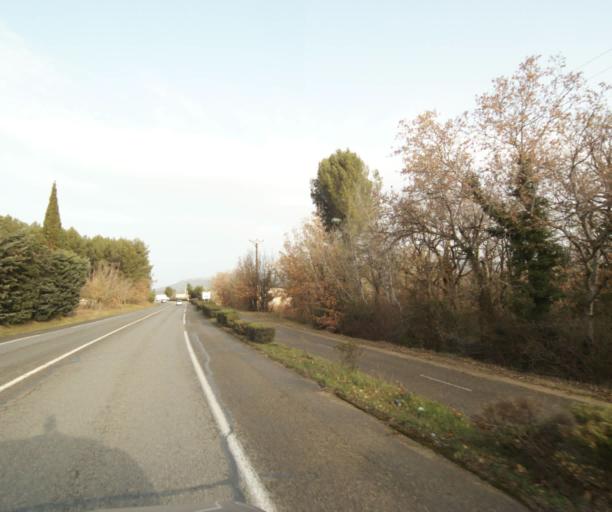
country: FR
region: Provence-Alpes-Cote d'Azur
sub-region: Departement des Bouches-du-Rhone
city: Rousset
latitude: 43.4611
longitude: 5.6225
